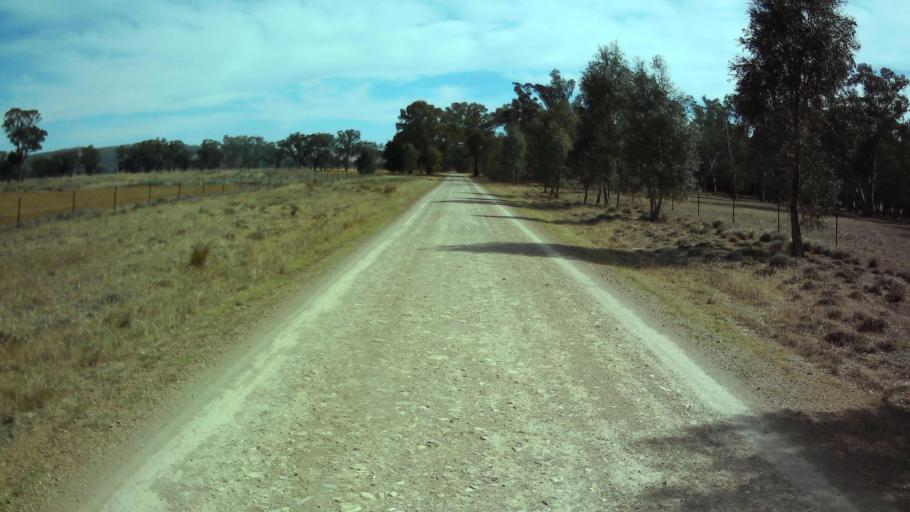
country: AU
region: New South Wales
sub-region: Weddin
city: Grenfell
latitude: -33.7039
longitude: 148.3016
